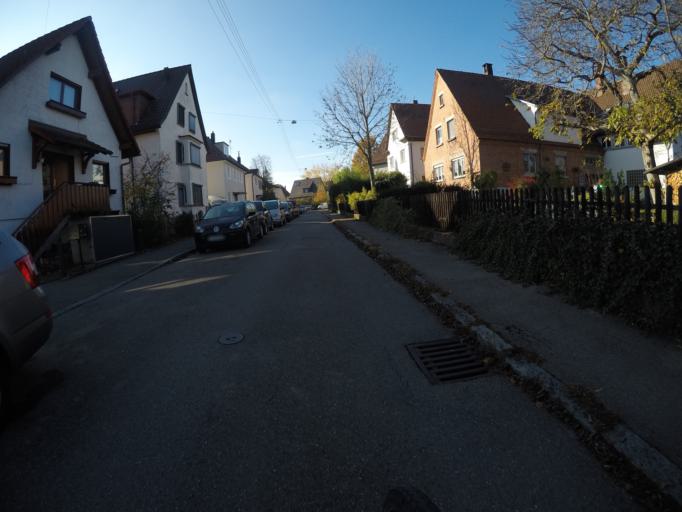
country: DE
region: Baden-Wuerttemberg
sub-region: Regierungsbezirk Stuttgart
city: Steinenbronn
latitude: 48.7343
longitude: 9.1132
